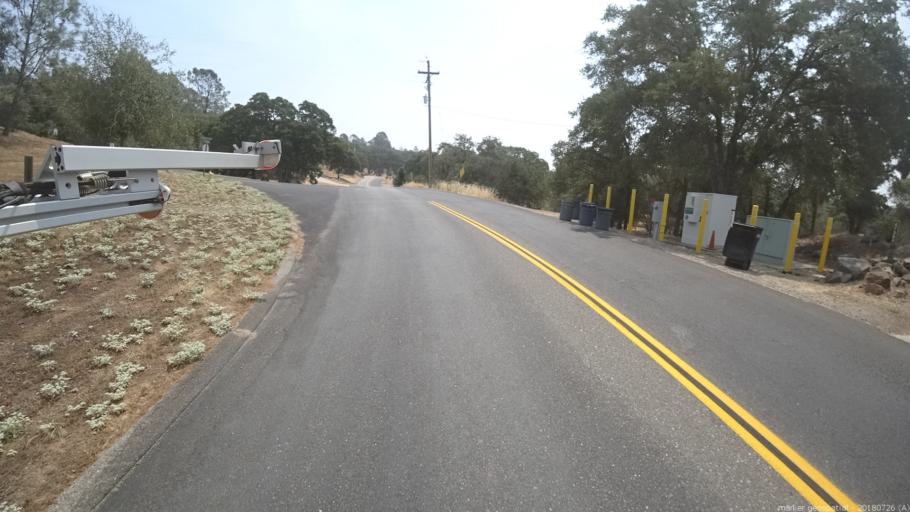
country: US
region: California
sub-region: Madera County
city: Coarsegold
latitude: 37.2445
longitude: -119.6844
